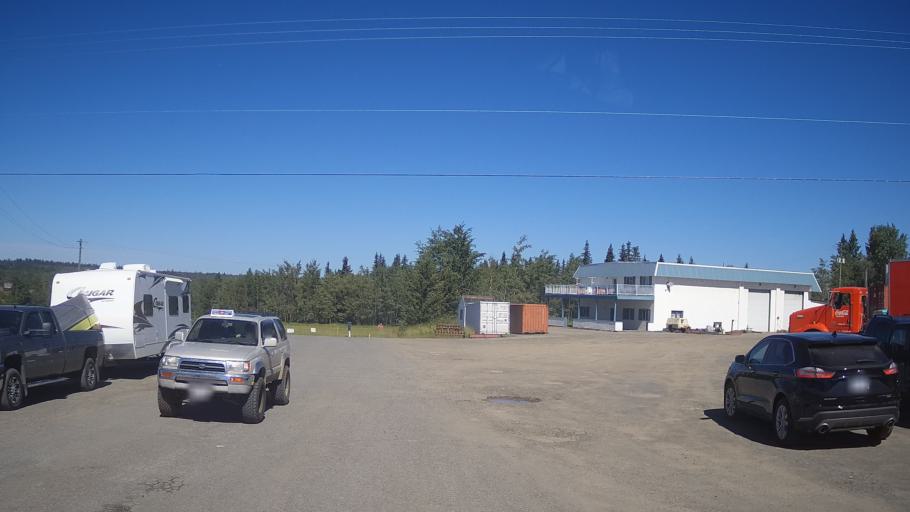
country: CA
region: British Columbia
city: Cache Creek
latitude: 51.5467
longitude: -120.9145
